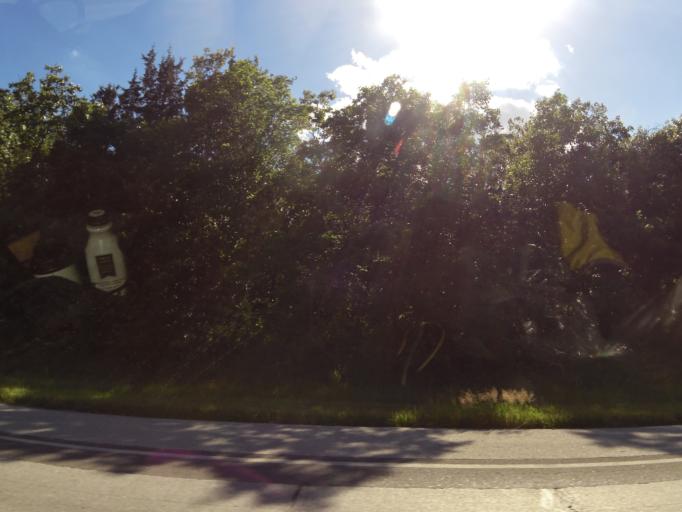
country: US
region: Missouri
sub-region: Lewis County
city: Canton
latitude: 40.0560
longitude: -91.5260
